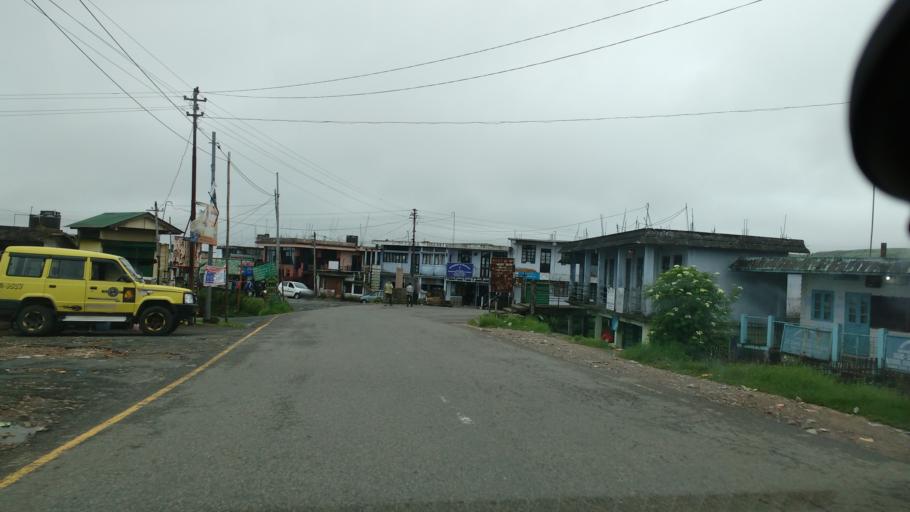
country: IN
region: Meghalaya
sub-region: East Khasi Hills
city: Cherrapunji
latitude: 25.2708
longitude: 91.7326
